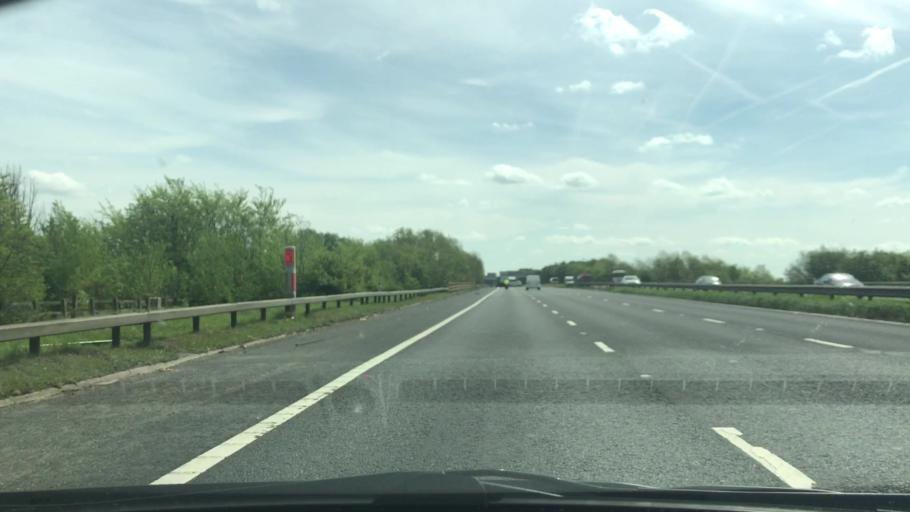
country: GB
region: England
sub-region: City and Borough of Wakefield
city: Knottingley
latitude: 53.6958
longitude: -1.2672
